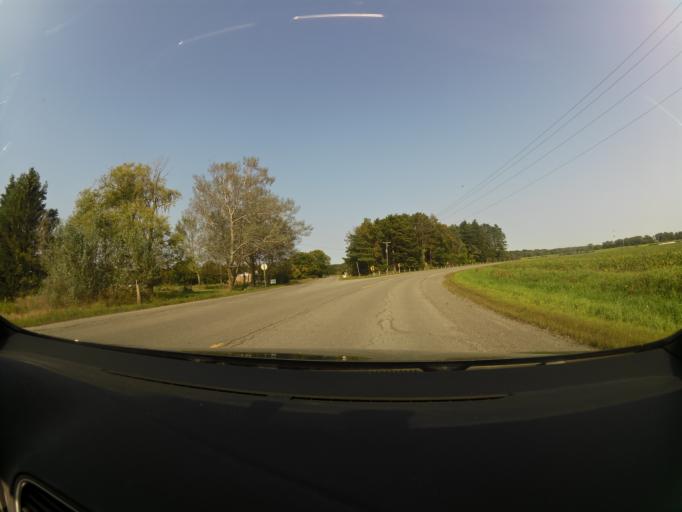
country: CA
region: Ontario
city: Carleton Place
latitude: 45.3456
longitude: -76.0643
